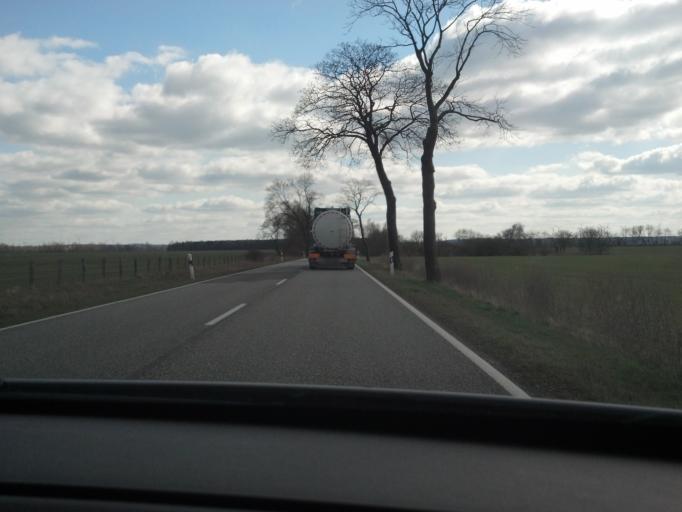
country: DE
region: Brandenburg
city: Gerdshagen
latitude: 53.3458
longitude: 12.2466
